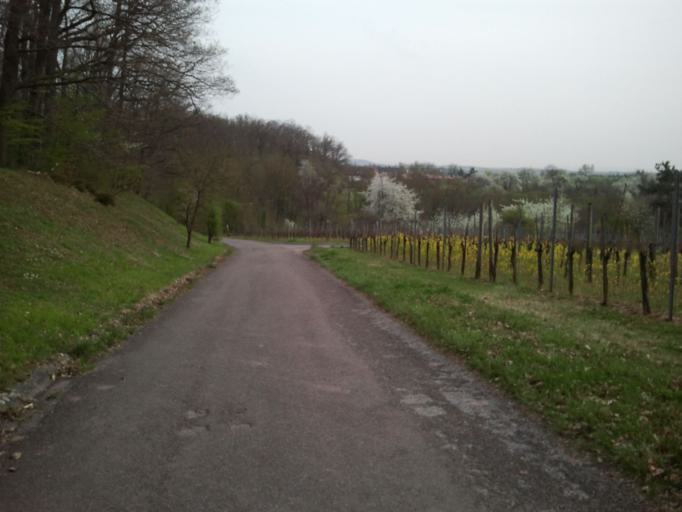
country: DE
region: Baden-Wuerttemberg
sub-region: Regierungsbezirk Stuttgart
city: Grossbottwar
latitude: 48.9833
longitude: 9.3095
